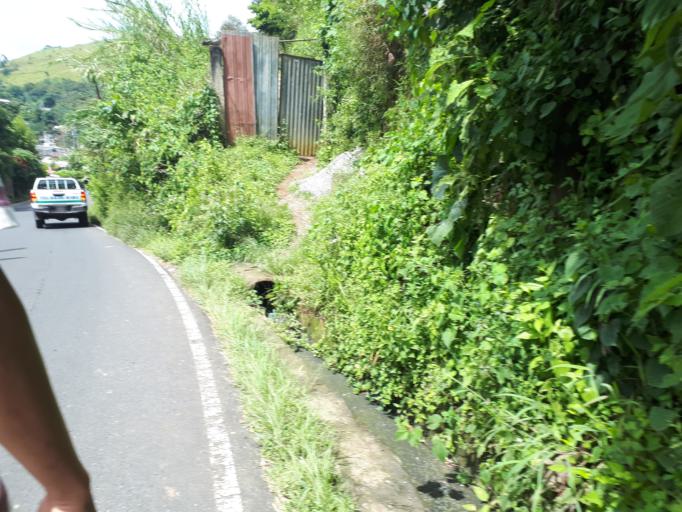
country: GT
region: Guatemala
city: Villa Canales
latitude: 14.4585
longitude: -90.5098
